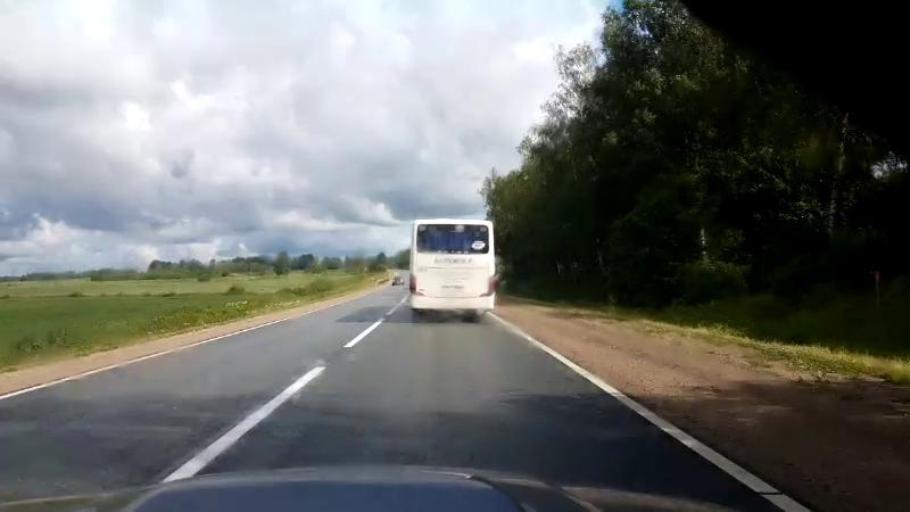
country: LV
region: Lecava
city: Iecava
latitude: 56.5191
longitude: 24.1730
